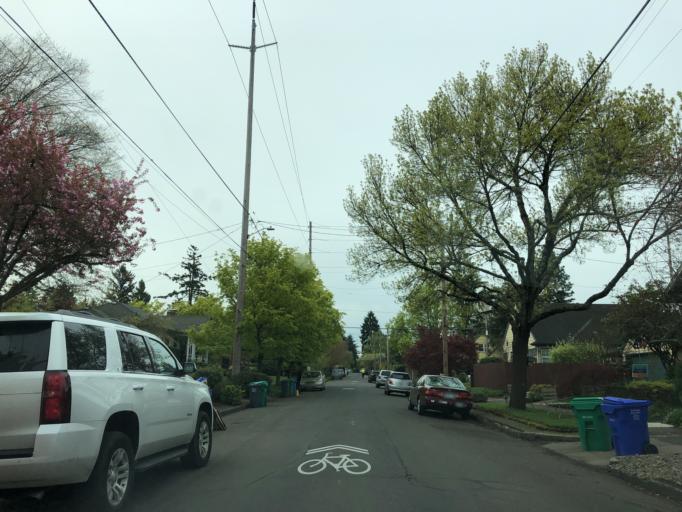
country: US
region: Oregon
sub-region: Multnomah County
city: Portland
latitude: 45.5549
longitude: -122.6328
